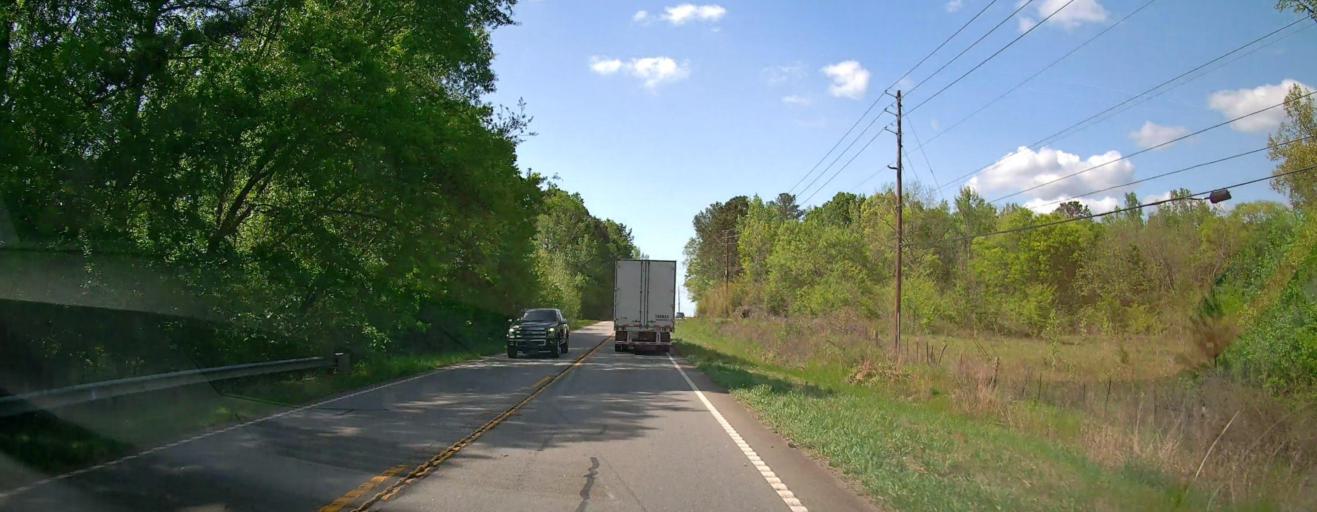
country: US
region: Georgia
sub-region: Greene County
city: Greensboro
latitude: 33.5064
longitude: -83.2259
